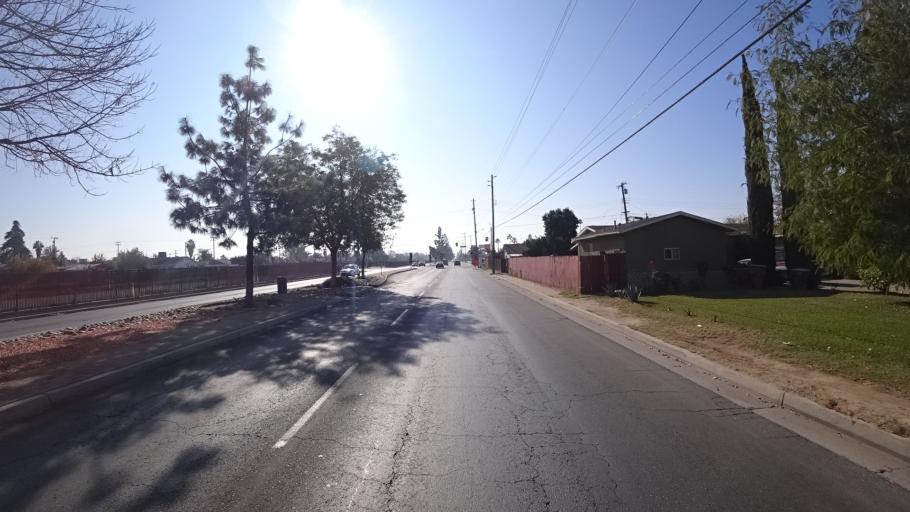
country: US
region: California
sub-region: Kern County
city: Bakersfield
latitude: 35.3331
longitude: -119.0213
